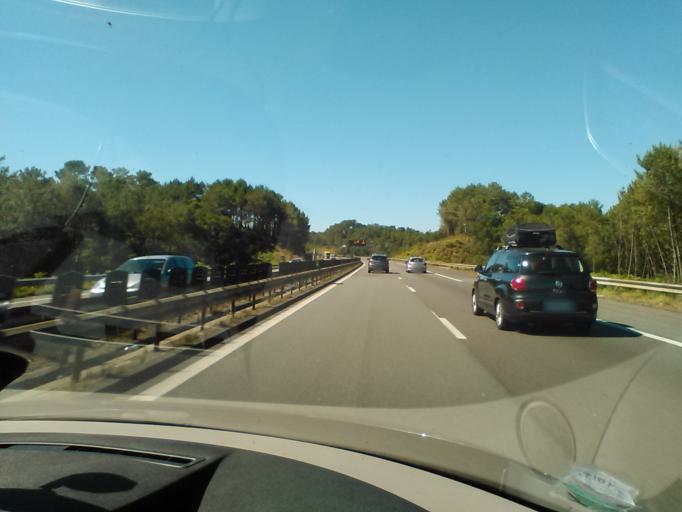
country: FR
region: Aquitaine
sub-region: Departement des Landes
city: Labenne
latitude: 43.5768
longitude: -1.4260
